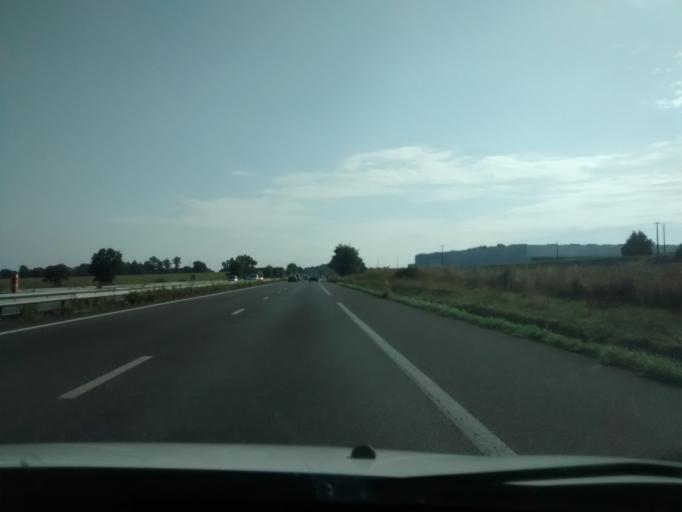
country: FR
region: Brittany
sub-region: Departement d'Ille-et-Vilaine
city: Argentre-du-Plessis
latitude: 48.0773
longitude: -1.1456
